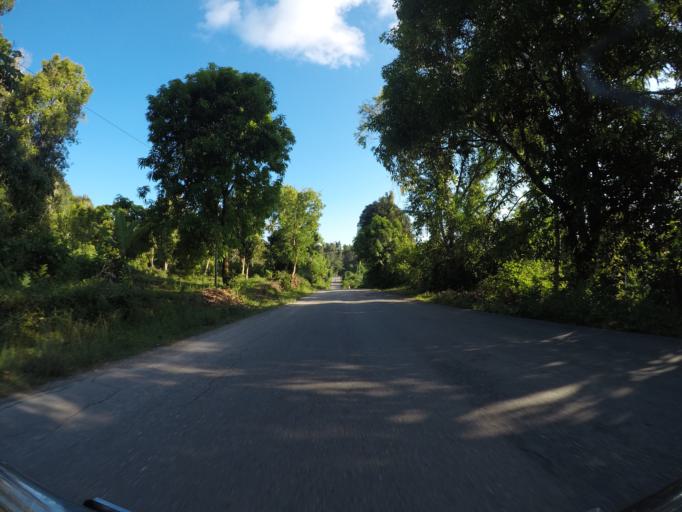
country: TZ
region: Pemba South
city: Mtambile
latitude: -5.3656
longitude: 39.7110
